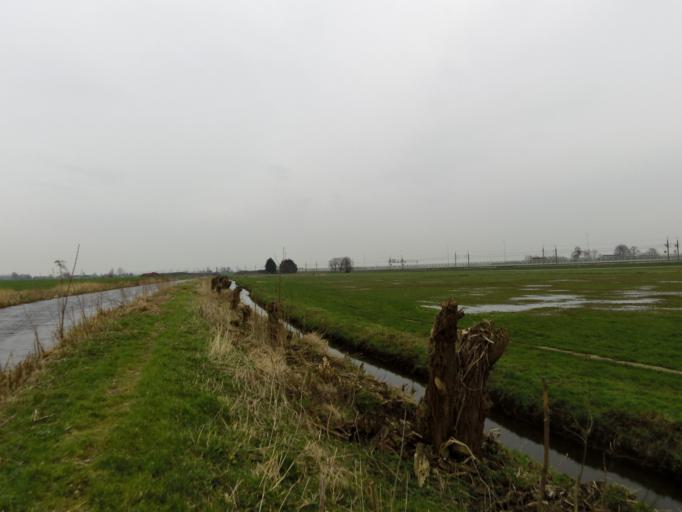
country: NL
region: South Holland
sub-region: Gemeente Leiderdorp
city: Leiderdorp
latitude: 52.1773
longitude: 4.5755
